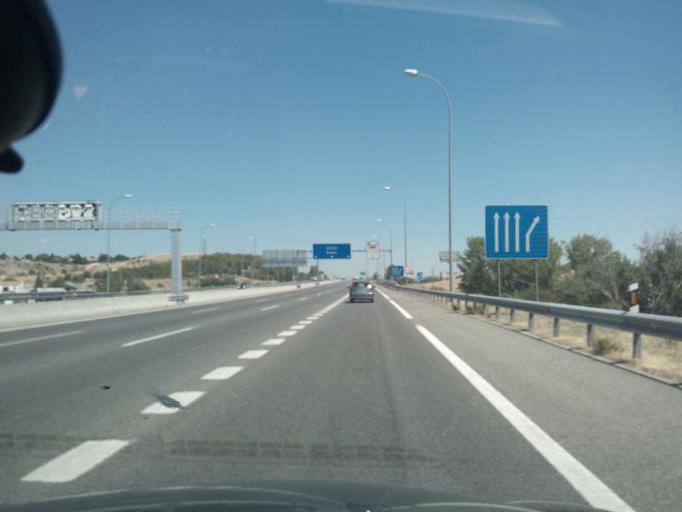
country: ES
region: Madrid
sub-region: Provincia de Madrid
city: San Sebastian de los Reyes
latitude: 40.5751
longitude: -3.5860
